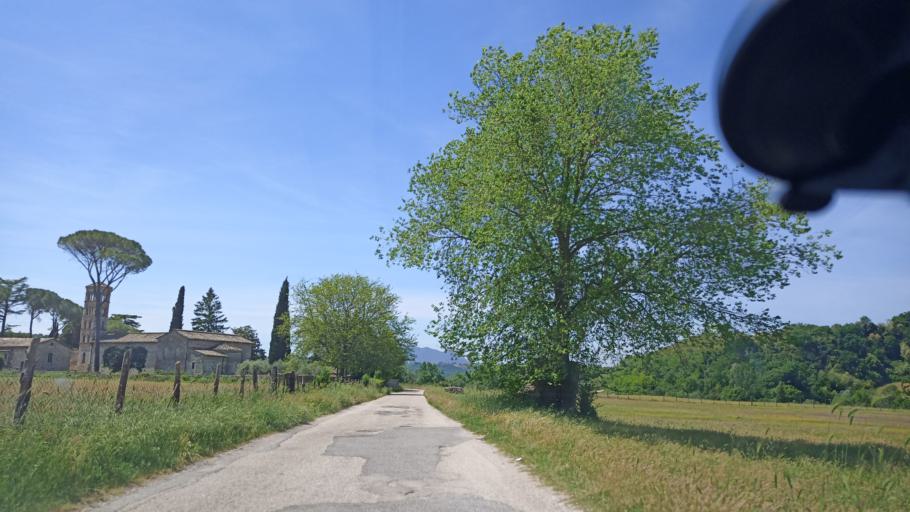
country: IT
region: Latium
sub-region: Provincia di Rieti
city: Tarano
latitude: 42.3328
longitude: 12.6054
